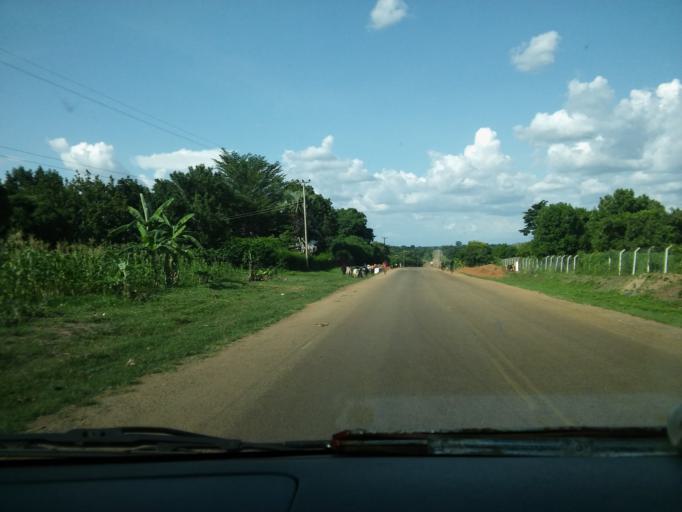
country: UG
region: Eastern Region
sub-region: Kibuku District
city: Kibuku
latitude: 1.0067
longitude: 33.7787
